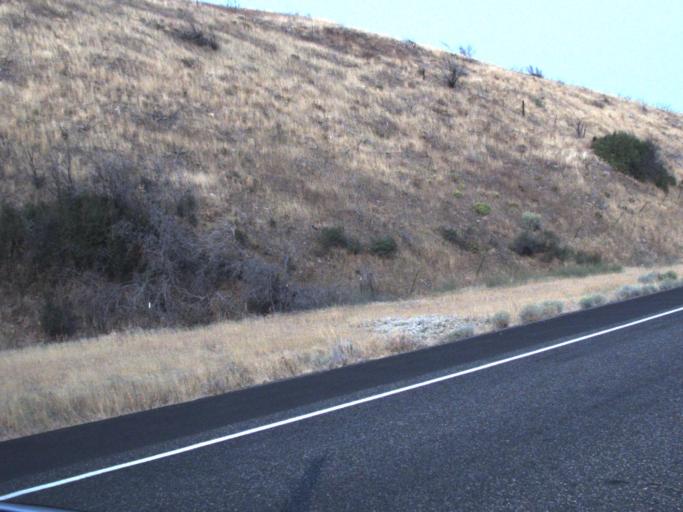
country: US
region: Washington
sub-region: Kittitas County
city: Ellensburg
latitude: 47.0846
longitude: -120.6441
